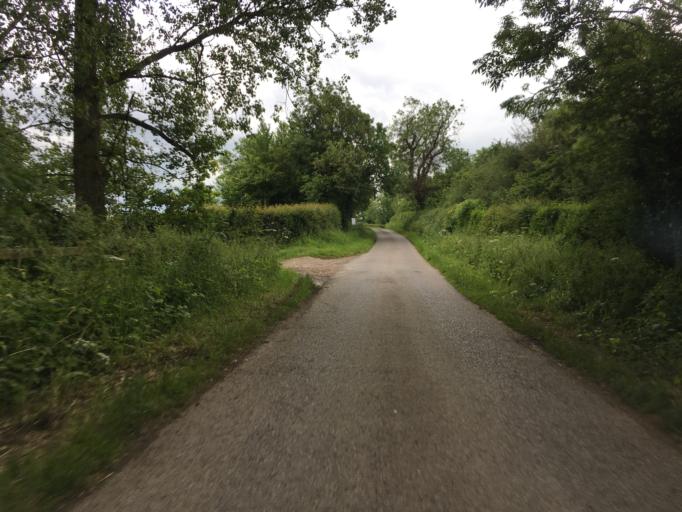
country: GB
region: England
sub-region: Gloucestershire
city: Coates
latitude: 51.6695
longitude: -2.0175
